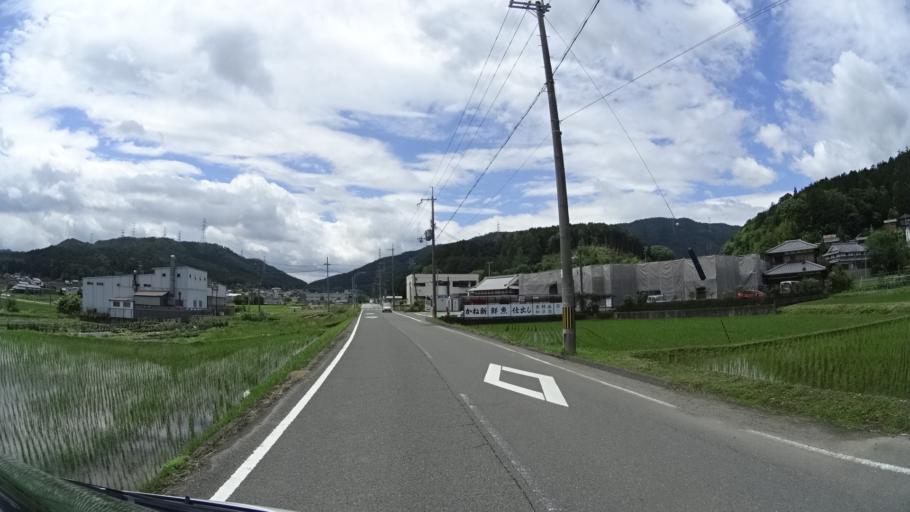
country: JP
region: Kyoto
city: Kameoka
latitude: 35.0105
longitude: 135.4822
